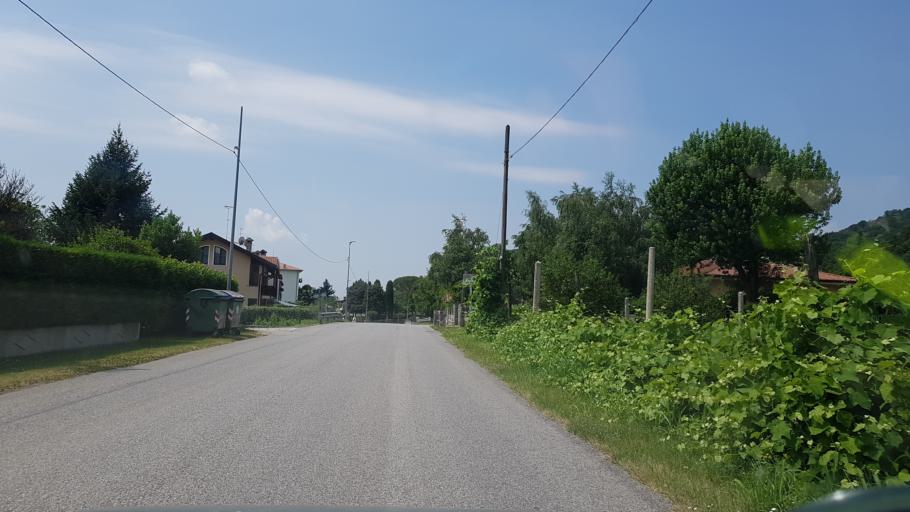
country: IT
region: Friuli Venezia Giulia
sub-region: Provincia di Udine
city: Torreano
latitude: 46.1254
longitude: 13.4274
